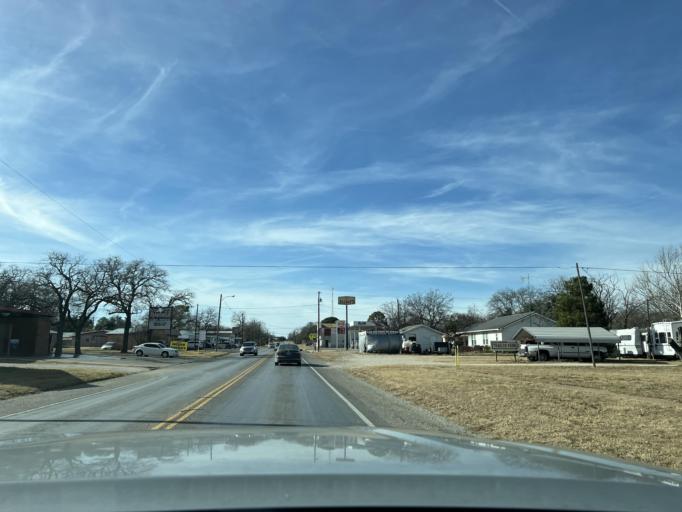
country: US
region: Texas
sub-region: Eastland County
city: Eastland
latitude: 32.4018
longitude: -98.8271
